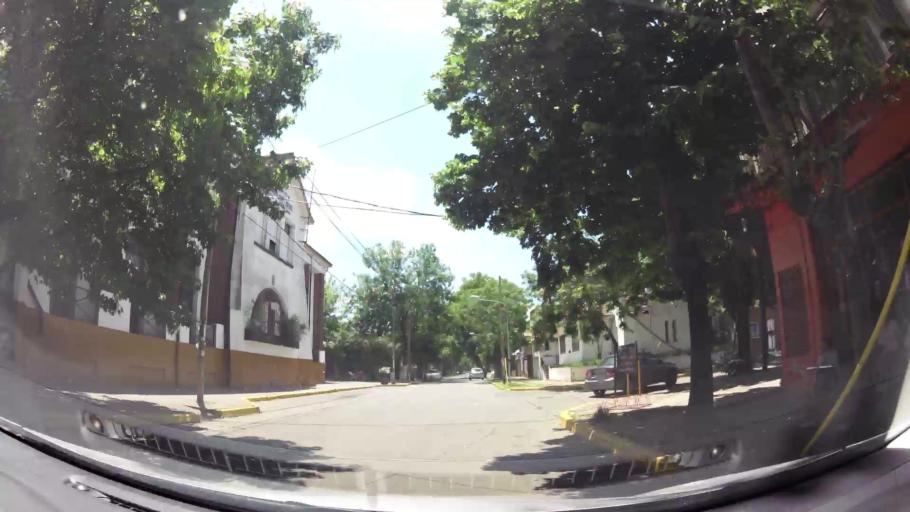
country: AR
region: Buenos Aires
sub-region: Partido de Tigre
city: Tigre
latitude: -34.4161
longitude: -58.5862
